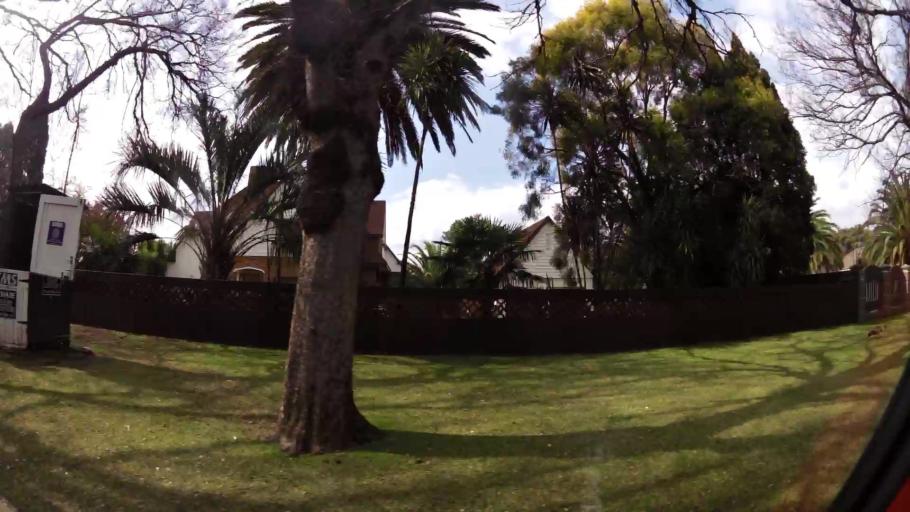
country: ZA
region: Gauteng
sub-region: Sedibeng District Municipality
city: Vanderbijlpark
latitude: -26.7377
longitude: 27.8362
